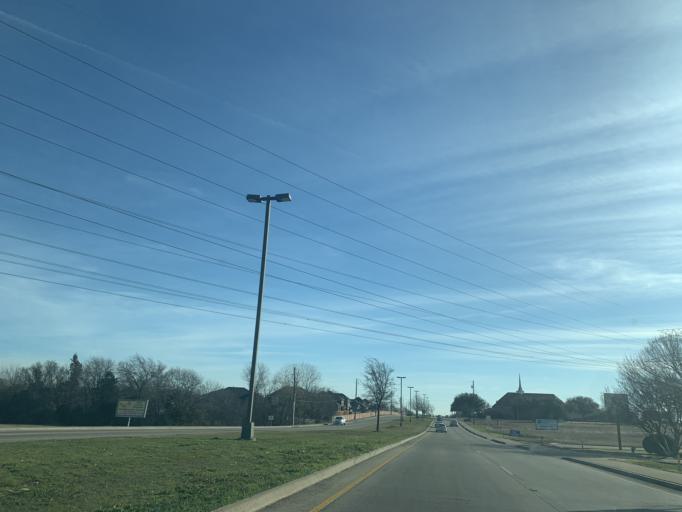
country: US
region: Texas
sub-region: Dallas County
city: Shamrock
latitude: 32.5897
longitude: -96.8908
